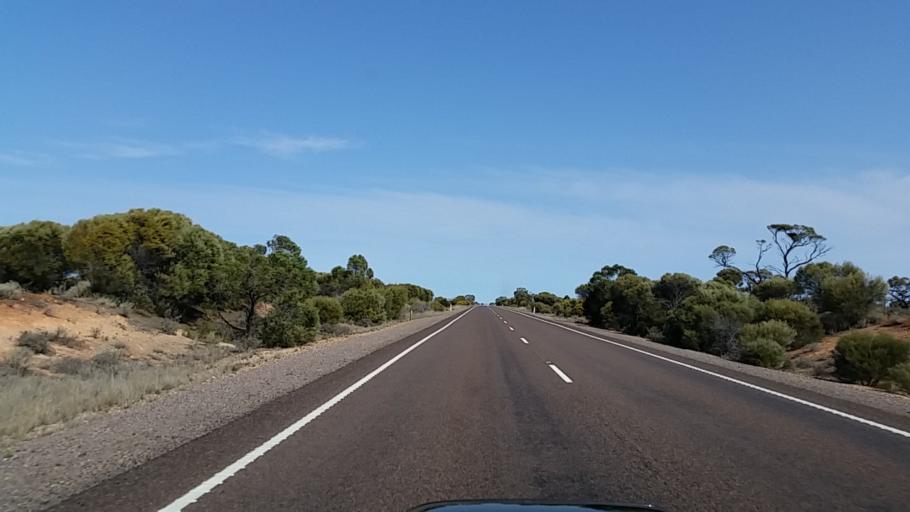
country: AU
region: South Australia
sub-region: Whyalla
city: Whyalla
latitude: -32.7745
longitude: 137.5318
